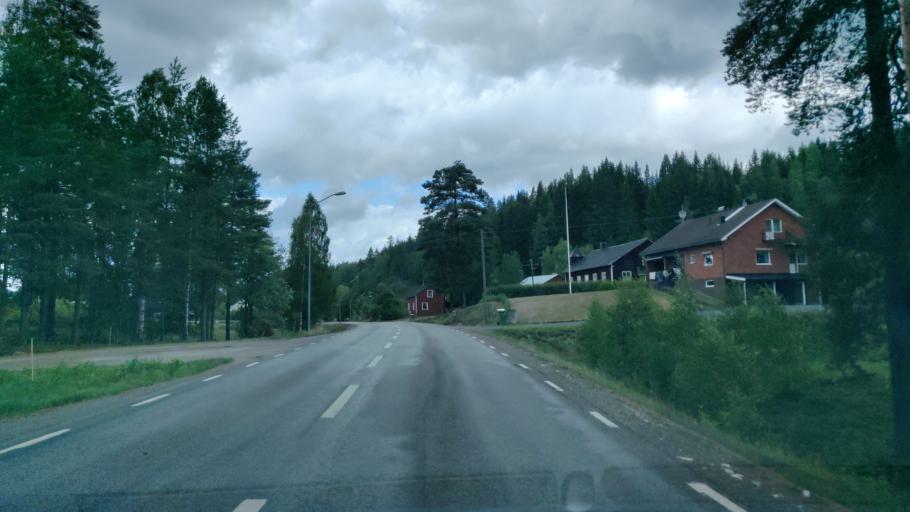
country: SE
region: Vaermland
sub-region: Torsby Kommun
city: Torsby
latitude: 60.6167
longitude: 13.0403
